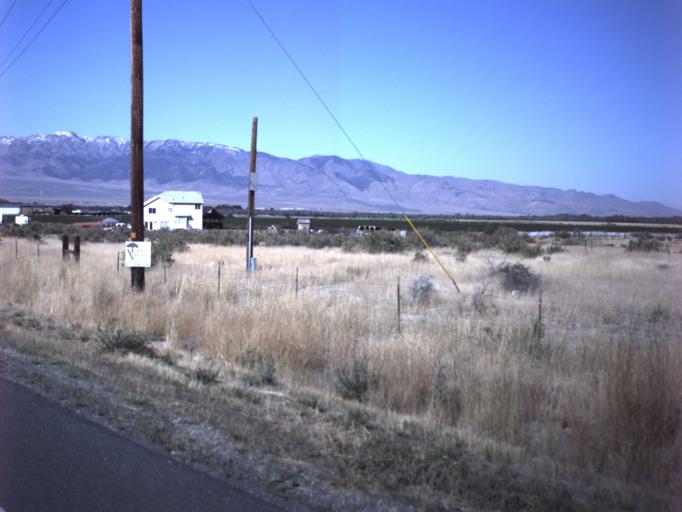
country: US
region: Utah
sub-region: Tooele County
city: Grantsville
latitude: 40.6003
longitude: -112.4087
